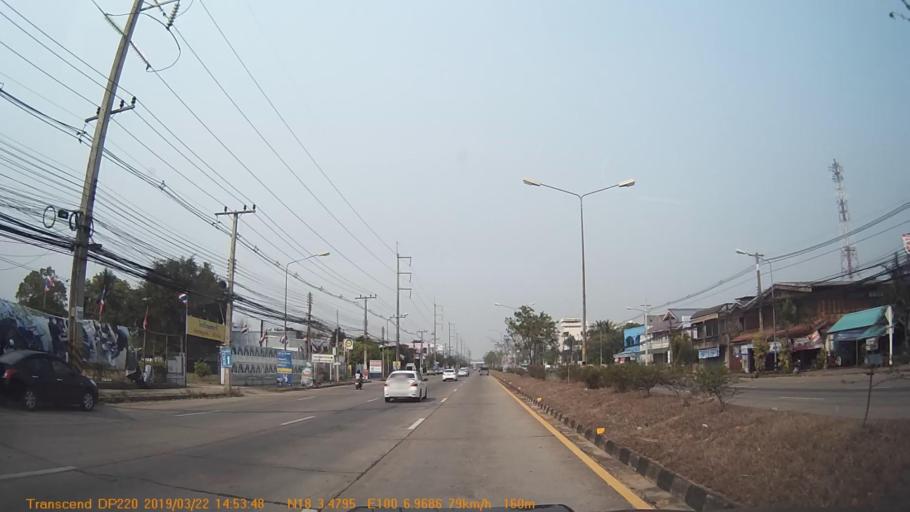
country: TH
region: Phrae
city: Sung Men
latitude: 18.0584
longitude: 100.1163
